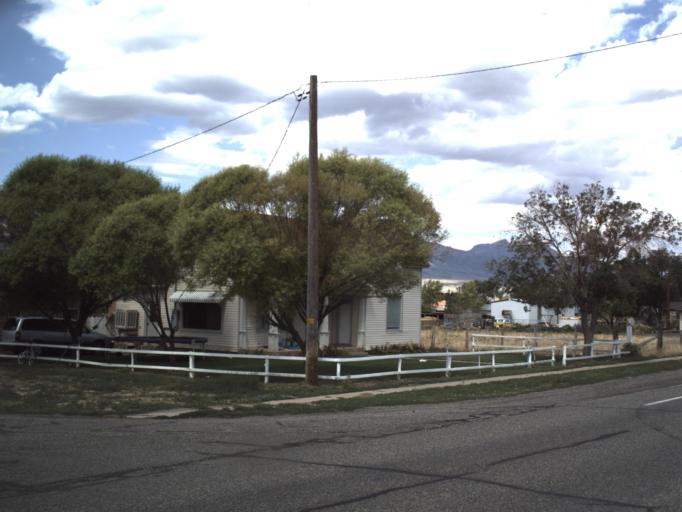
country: US
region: Utah
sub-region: Sanpete County
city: Gunnison
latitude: 39.2397
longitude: -112.1038
